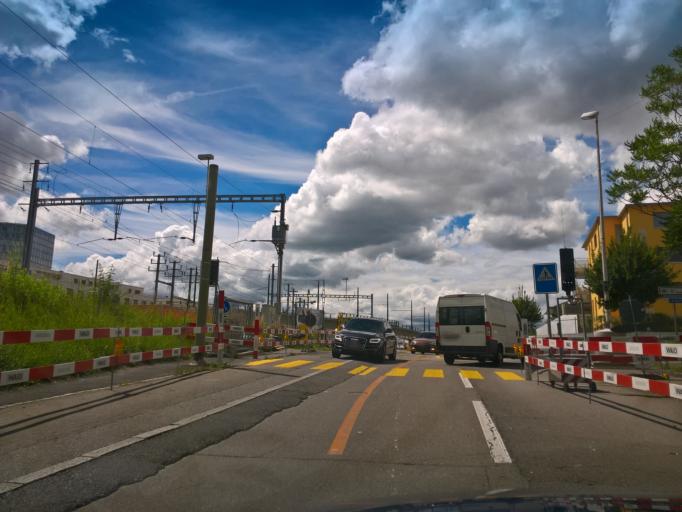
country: CH
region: Zurich
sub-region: Bezirk Buelach
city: Wallisellen / Wallisellen-Ost
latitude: 47.4110
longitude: 8.5994
